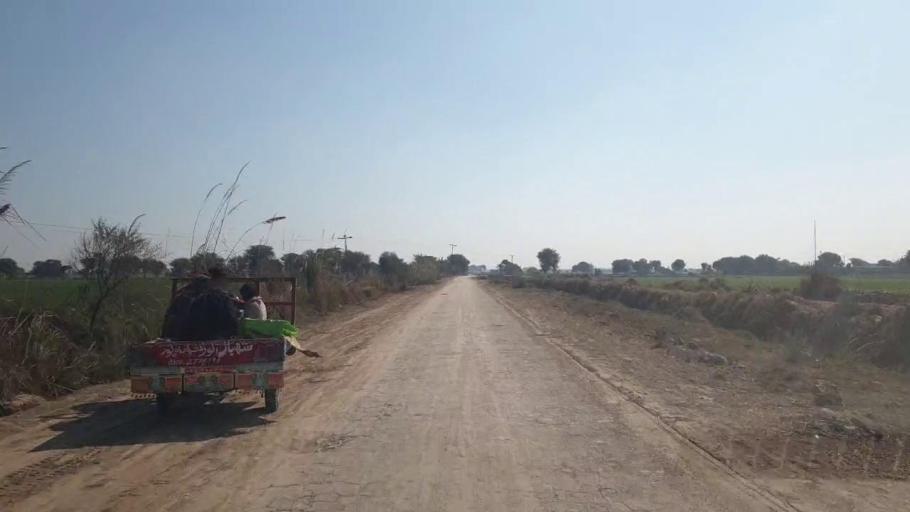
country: PK
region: Sindh
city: Shahdadpur
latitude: 25.9507
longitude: 68.6312
